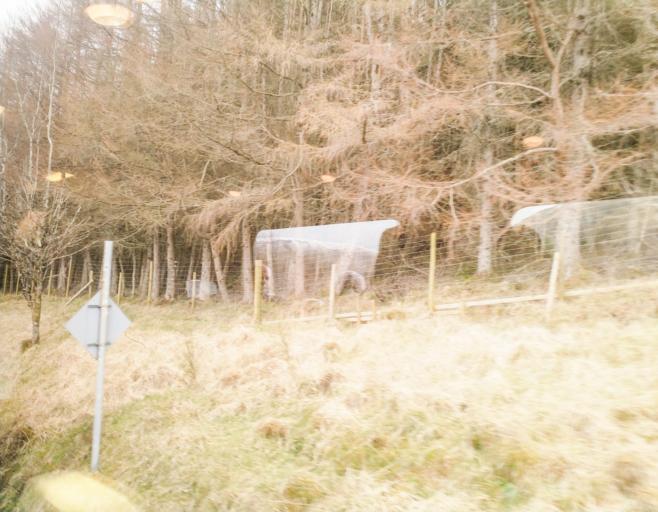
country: GB
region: Scotland
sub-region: Argyll and Bute
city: Garelochhead
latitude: 56.4362
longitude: -4.7050
